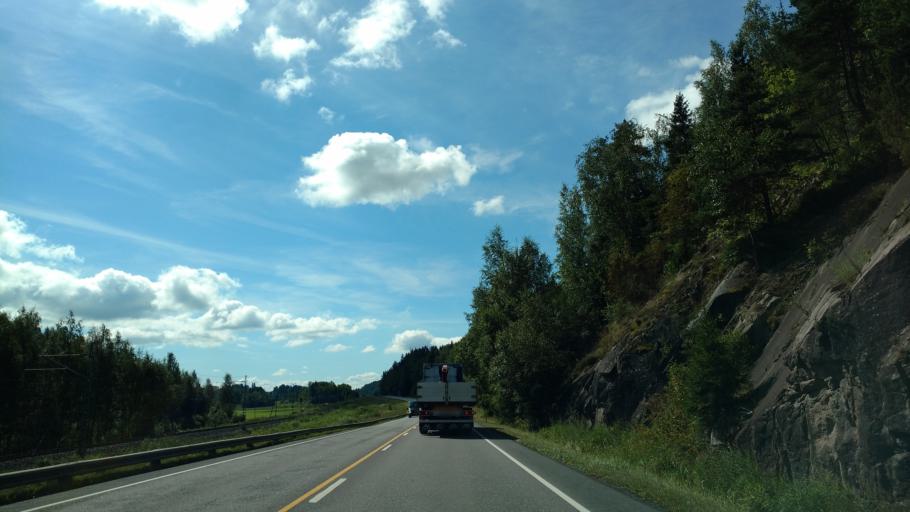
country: FI
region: Varsinais-Suomi
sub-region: Salo
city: Pernioe
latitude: 60.2886
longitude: 23.1145
